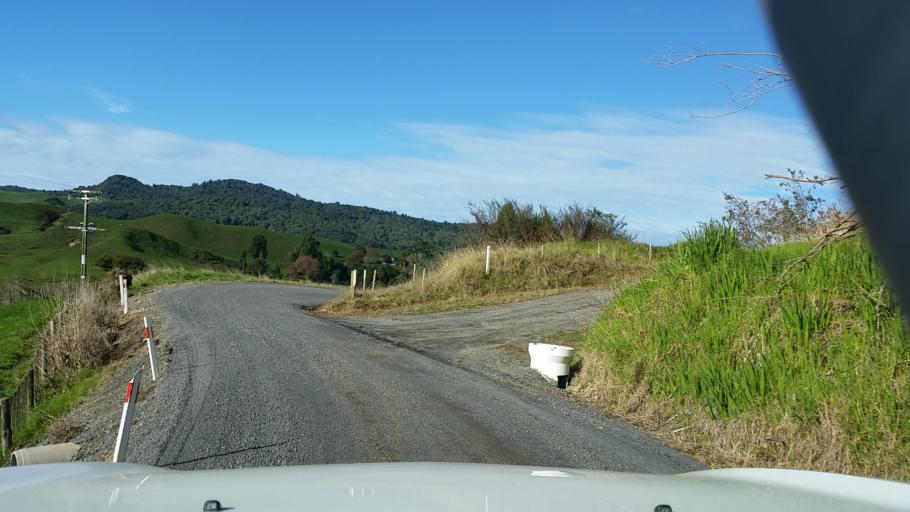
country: NZ
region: Waikato
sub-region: Matamata-Piako District
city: Matamata
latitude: -37.8073
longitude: 175.6353
